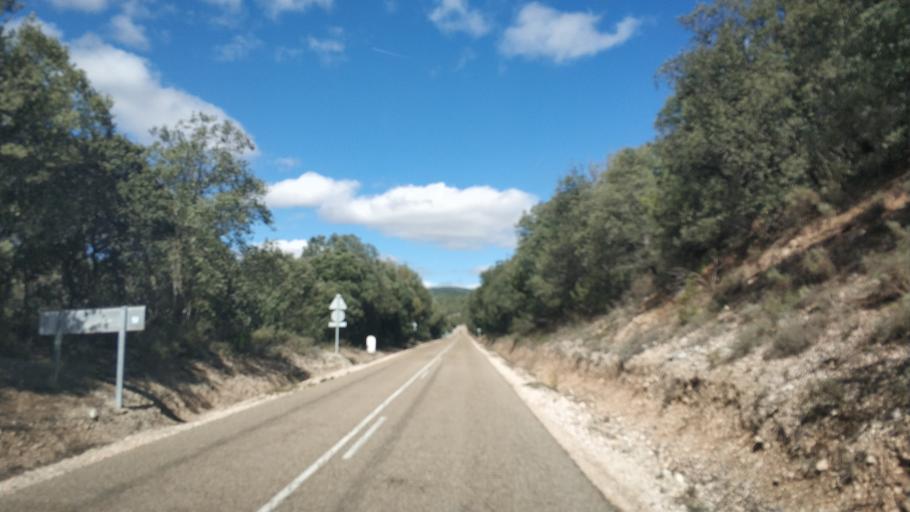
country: ES
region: Castille and Leon
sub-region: Provincia de Burgos
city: Retuerta
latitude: 42.0384
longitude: -3.4782
